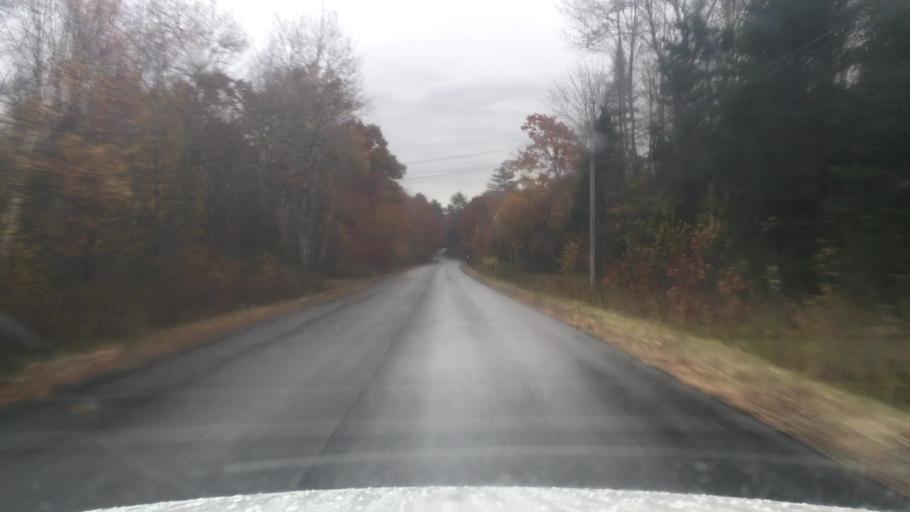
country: US
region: Maine
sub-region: Waldo County
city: Lincolnville
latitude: 44.3153
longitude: -69.0735
